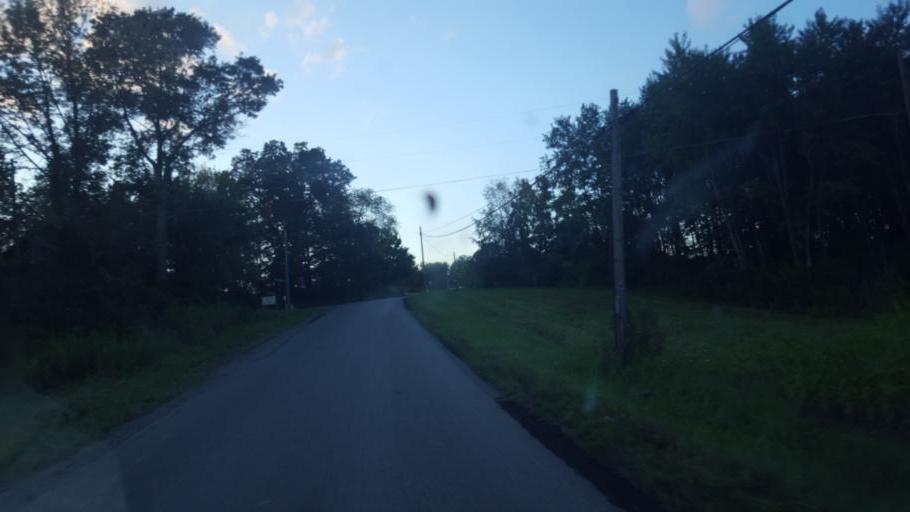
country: US
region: Pennsylvania
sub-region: Clarion County
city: Knox
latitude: 41.2169
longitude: -79.5413
